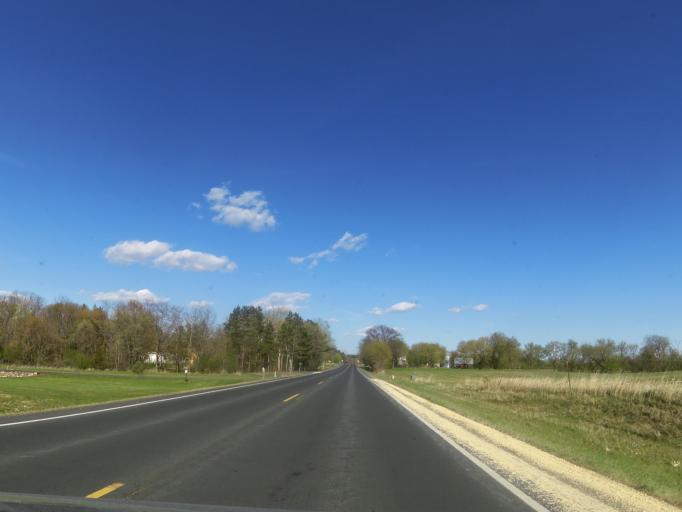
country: US
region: Minnesota
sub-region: Washington County
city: Oak Park Heights
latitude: 45.0607
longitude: -92.7638
